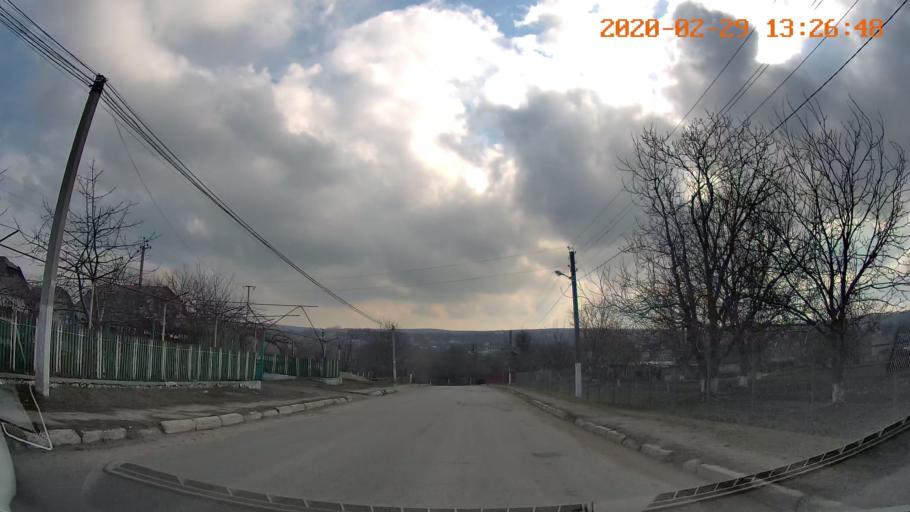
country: MD
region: Telenesti
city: Camenca
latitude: 47.9170
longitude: 28.6391
